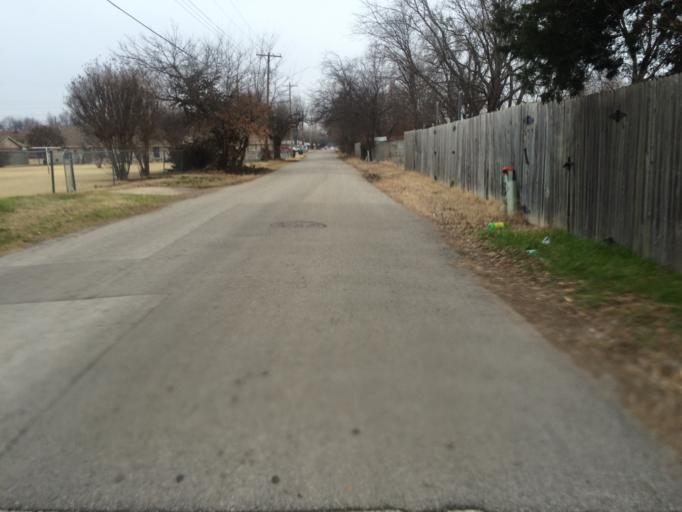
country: US
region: Oklahoma
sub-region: Cleveland County
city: Norman
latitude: 35.2049
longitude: -97.4280
